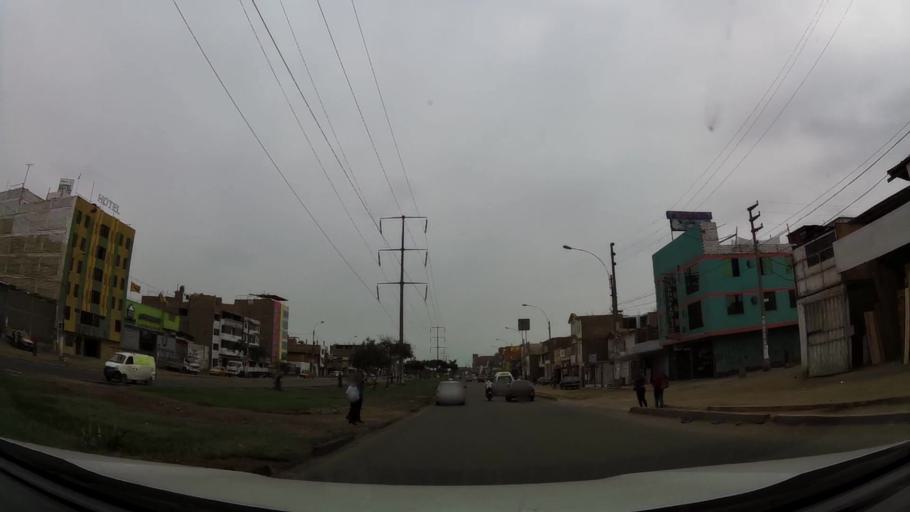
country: PE
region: Lima
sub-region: Lima
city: Independencia
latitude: -11.9854
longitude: -77.0793
